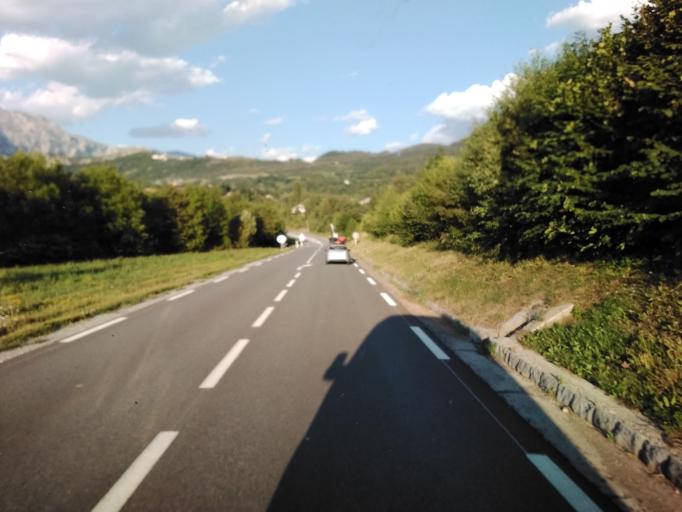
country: FR
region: Provence-Alpes-Cote d'Azur
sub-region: Departement des Alpes-de-Haute-Provence
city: Seyne-les-Alpes
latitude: 44.4434
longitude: 6.3468
